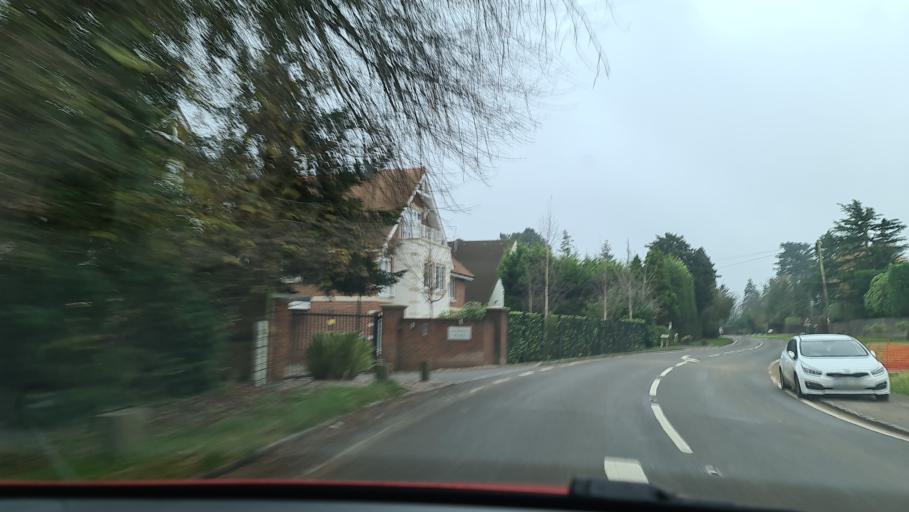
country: GB
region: England
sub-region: Buckinghamshire
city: Beaconsfield
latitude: 51.6284
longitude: -0.6558
